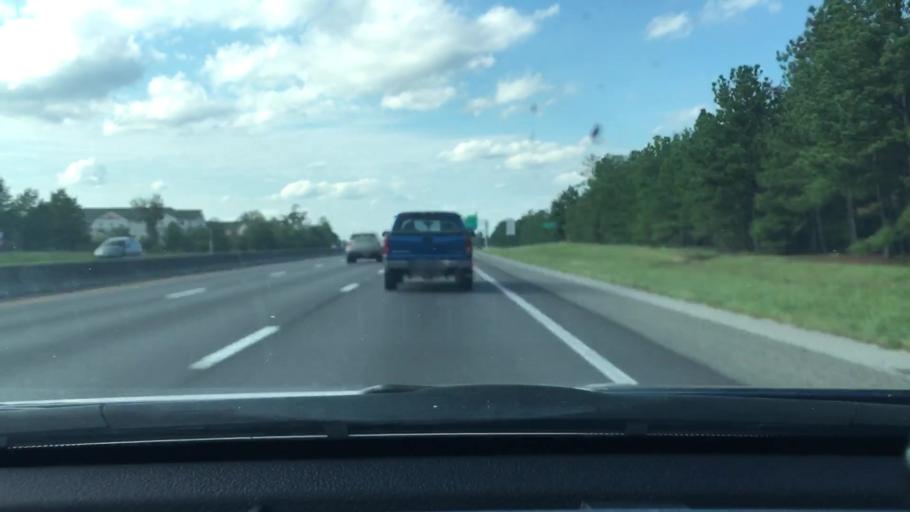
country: US
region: South Carolina
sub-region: Lexington County
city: Irmo
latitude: 34.0855
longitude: -81.1602
